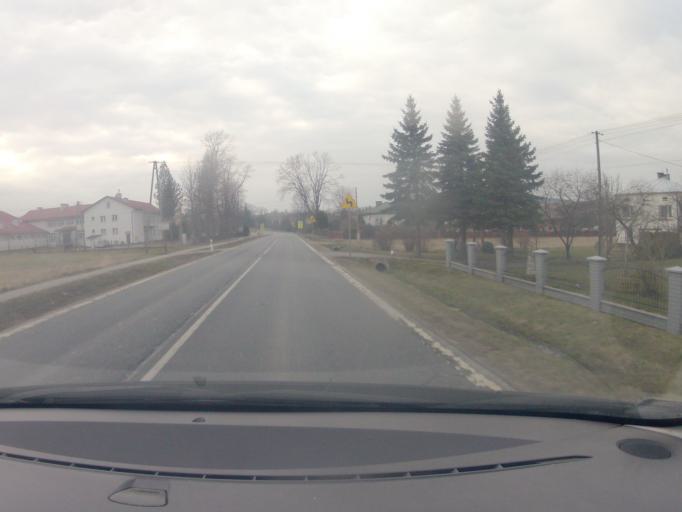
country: PL
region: Subcarpathian Voivodeship
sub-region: Powiat krosnienski
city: Dukla
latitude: 49.5592
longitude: 21.6249
